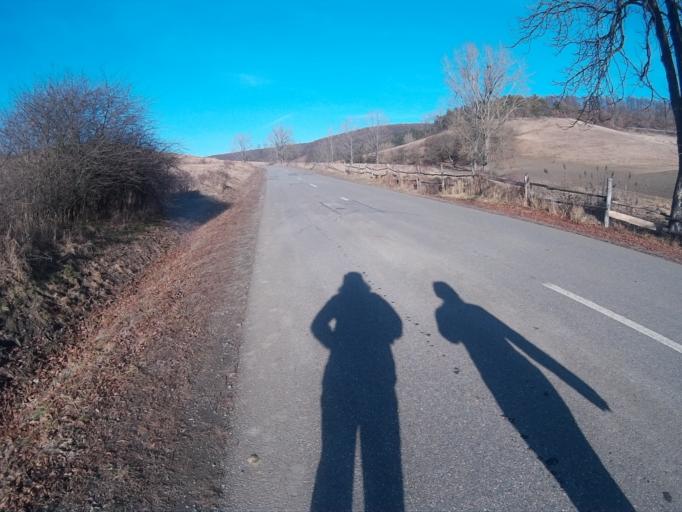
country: HU
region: Borsod-Abauj-Zemplen
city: Putnok
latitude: 48.3951
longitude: 20.4887
